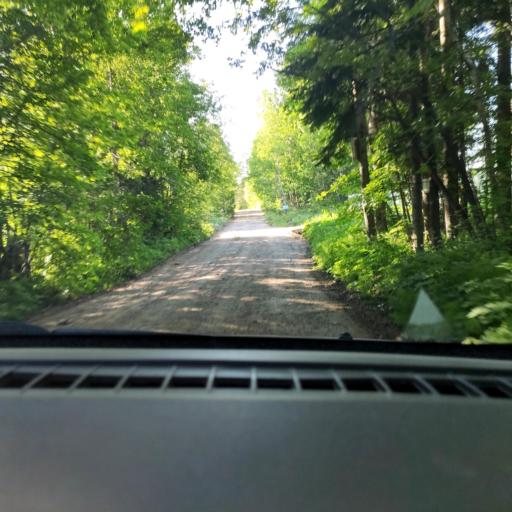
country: RU
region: Perm
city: Overyata
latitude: 58.1240
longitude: 55.8790
